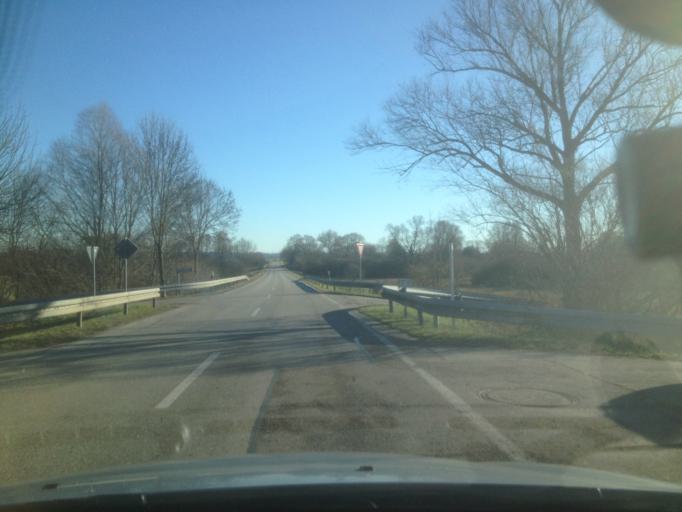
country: DE
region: Bavaria
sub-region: Upper Bavaria
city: Berglern
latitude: 48.4106
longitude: 11.9113
